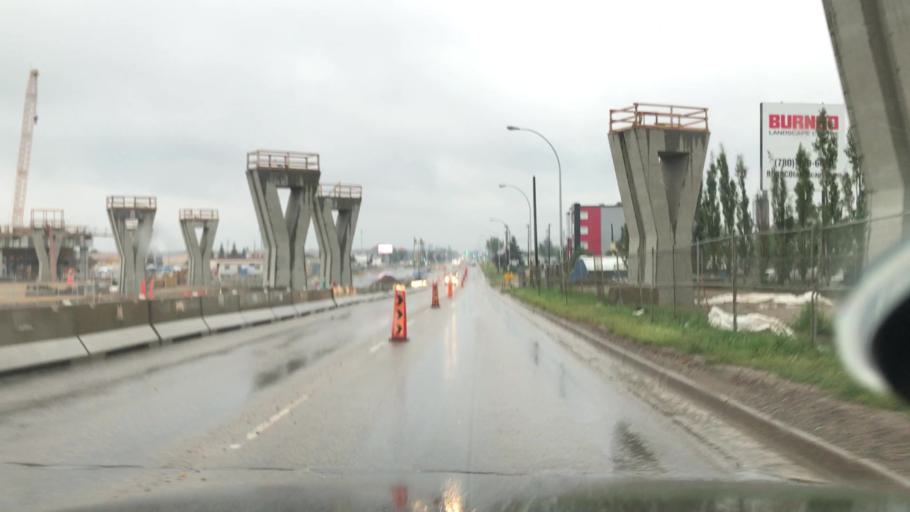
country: CA
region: Alberta
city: Edmonton
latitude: 53.4982
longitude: -113.4426
